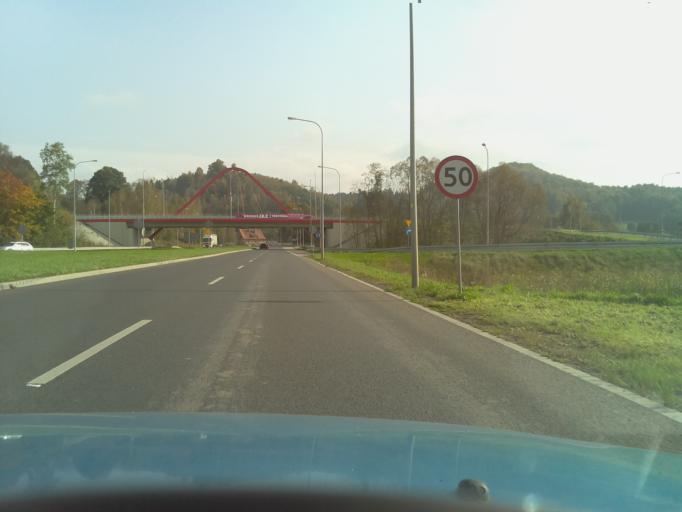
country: PL
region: Lower Silesian Voivodeship
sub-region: Powiat jeleniogorski
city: Jezow Sudecki
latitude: 50.9077
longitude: 15.7936
